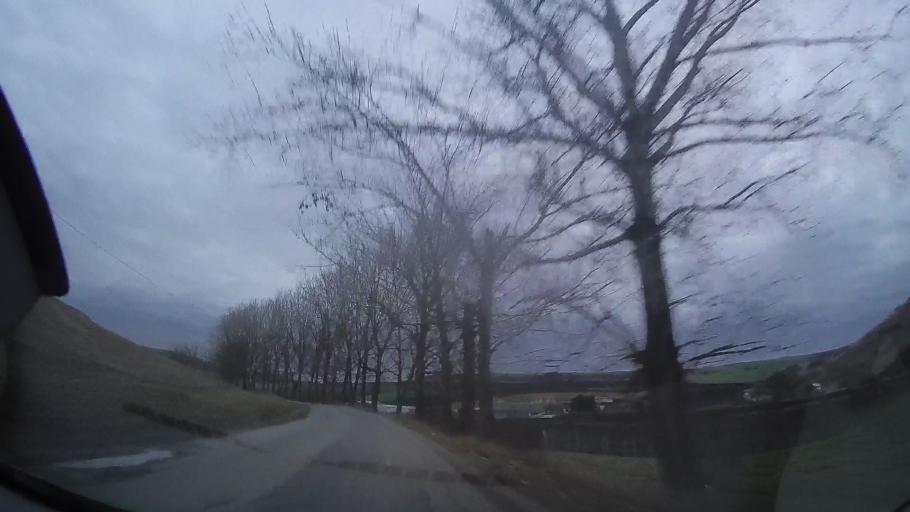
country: RO
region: Cluj
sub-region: Comuna Caianu
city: Vaida-Camaras
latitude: 46.8134
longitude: 23.9300
